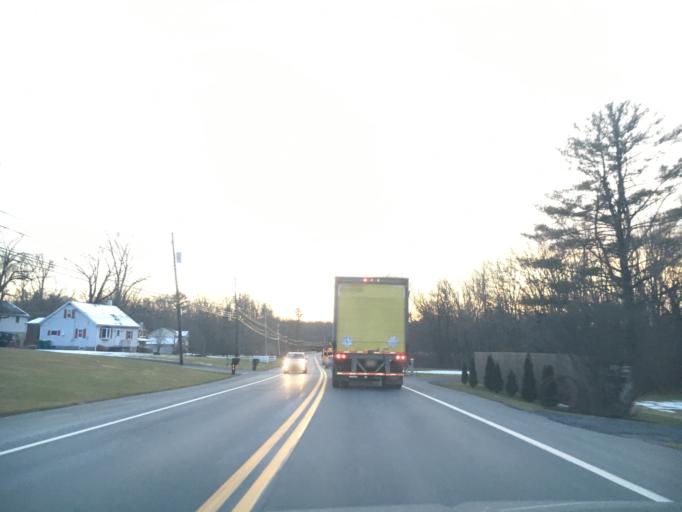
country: US
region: Pennsylvania
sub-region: Northampton County
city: Wind Gap
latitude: 40.8190
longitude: -75.3292
